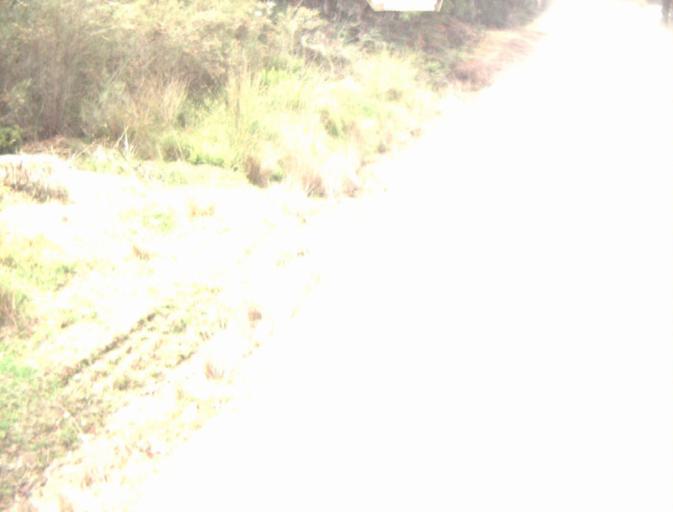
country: AU
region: Tasmania
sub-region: Northern Midlands
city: Evandale
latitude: -41.4525
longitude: 147.4814
